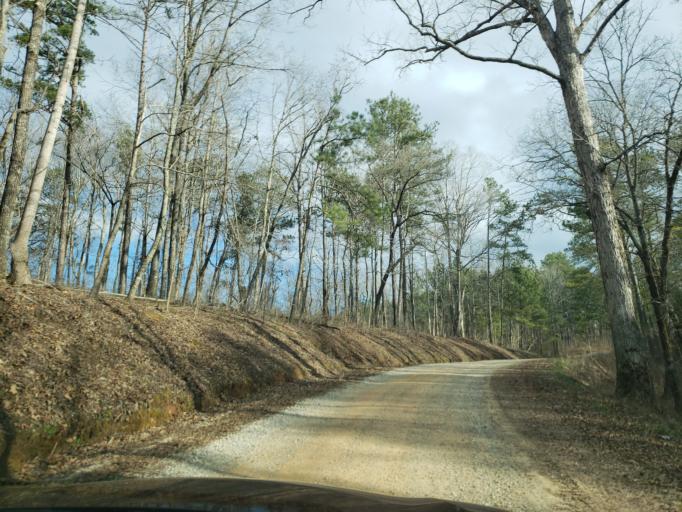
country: US
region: Alabama
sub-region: Cleburne County
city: Heflin
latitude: 33.6501
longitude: -85.6349
